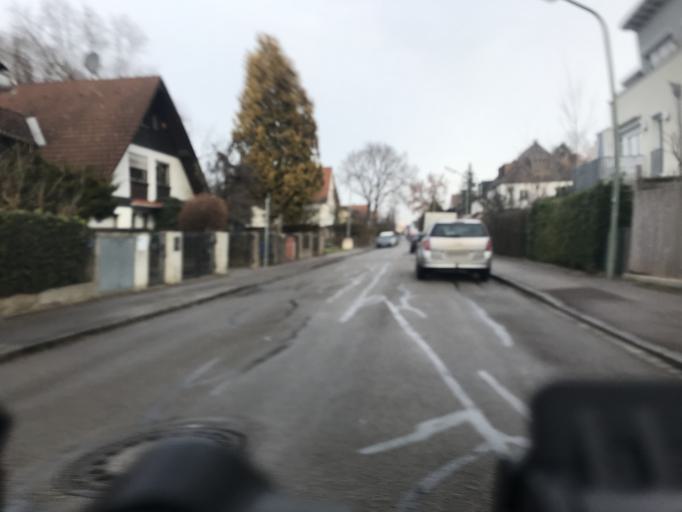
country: DE
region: Bavaria
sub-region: Upper Bavaria
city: Grafelfing
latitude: 48.1499
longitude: 11.4159
